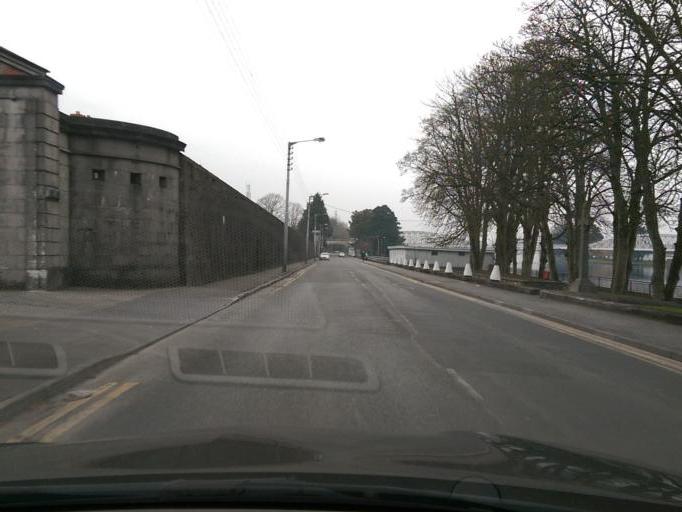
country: IE
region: Leinster
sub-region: An Iarmhi
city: Athlone
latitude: 53.4249
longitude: -7.9445
